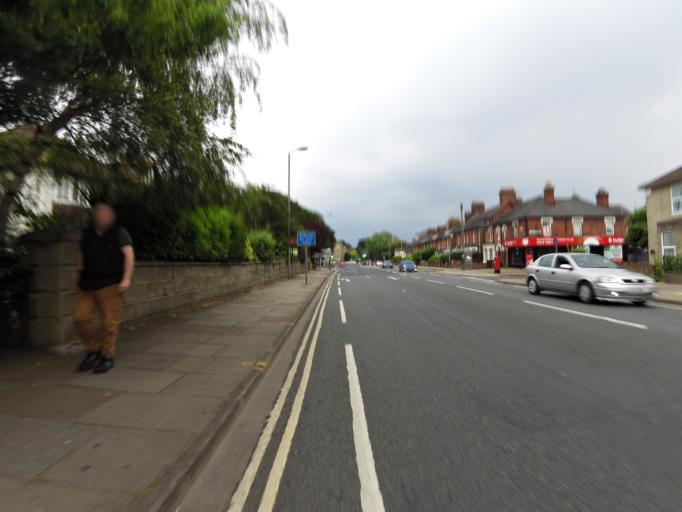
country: GB
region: England
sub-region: Suffolk
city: Ipswich
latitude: 52.0666
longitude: 1.1385
